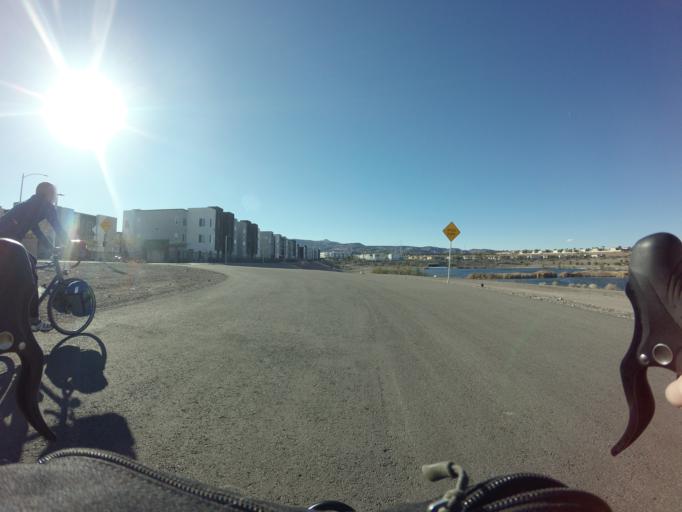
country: US
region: Nevada
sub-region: Clark County
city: Whitney
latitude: 36.0371
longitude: -115.0505
